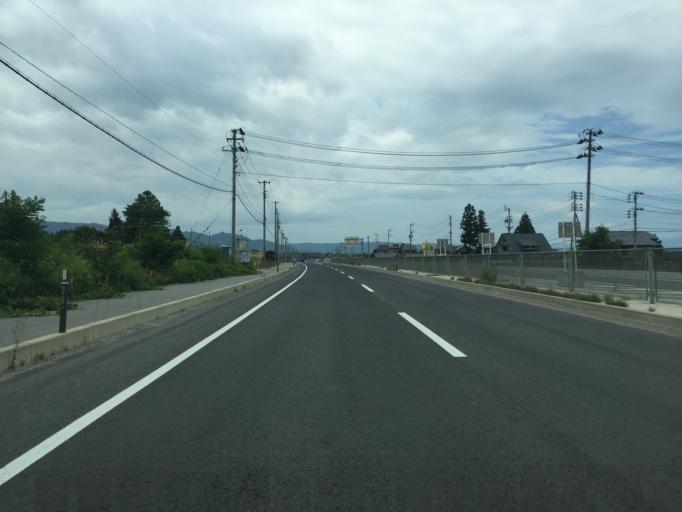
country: JP
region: Yamagata
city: Yonezawa
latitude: 37.8954
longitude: 140.1601
